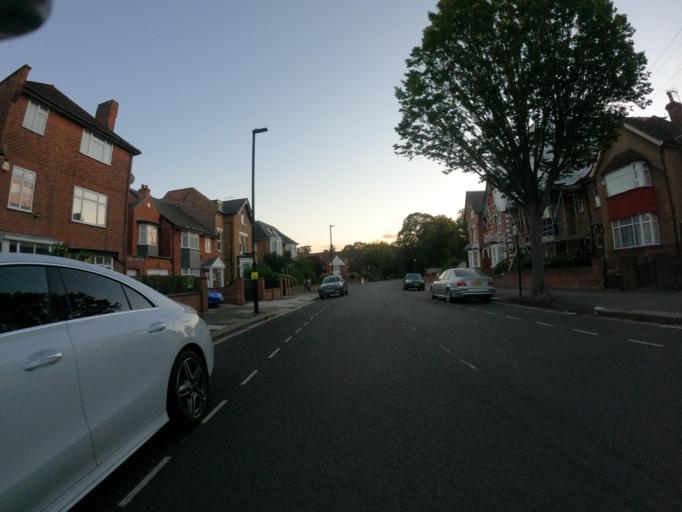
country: GB
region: England
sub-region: Greater London
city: Acton
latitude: 51.5142
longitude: -0.2777
